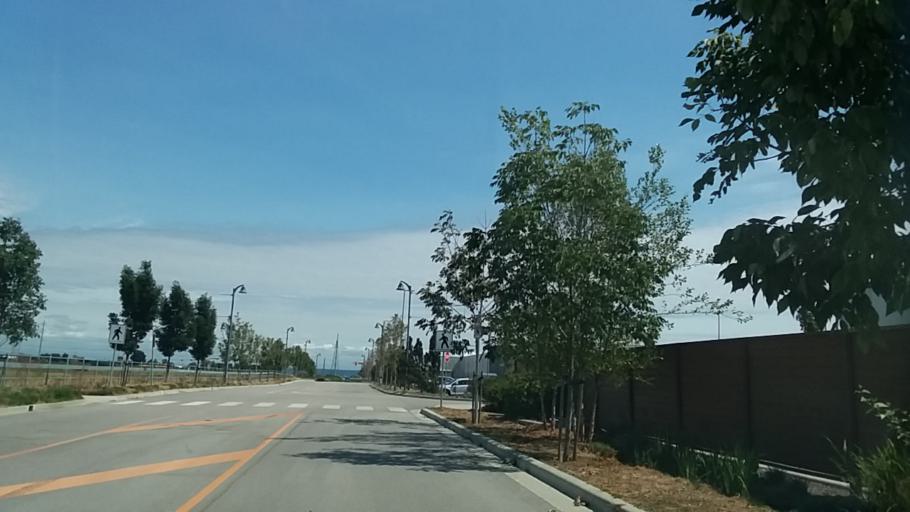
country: CA
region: British Columbia
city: Ladner
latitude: 49.0430
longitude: -123.0832
